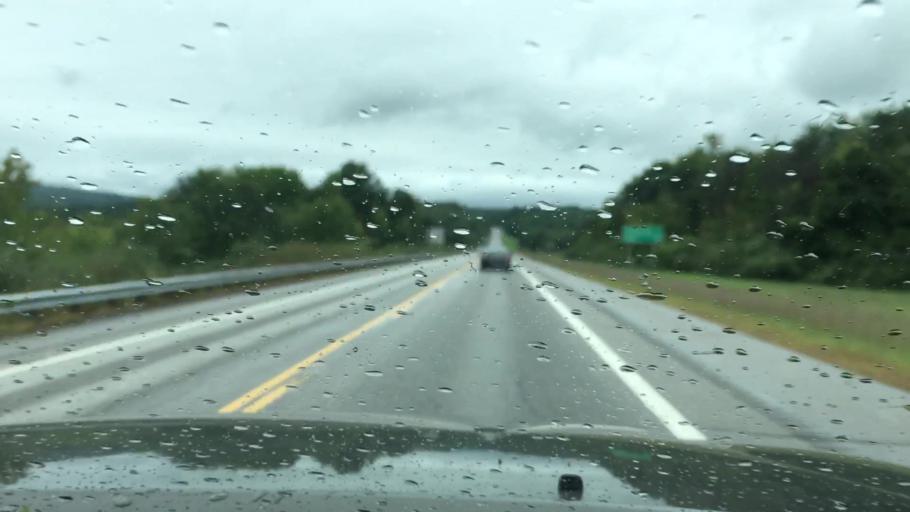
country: US
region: New Hampshire
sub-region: Merrimack County
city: Henniker
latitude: 43.1815
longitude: -71.8376
